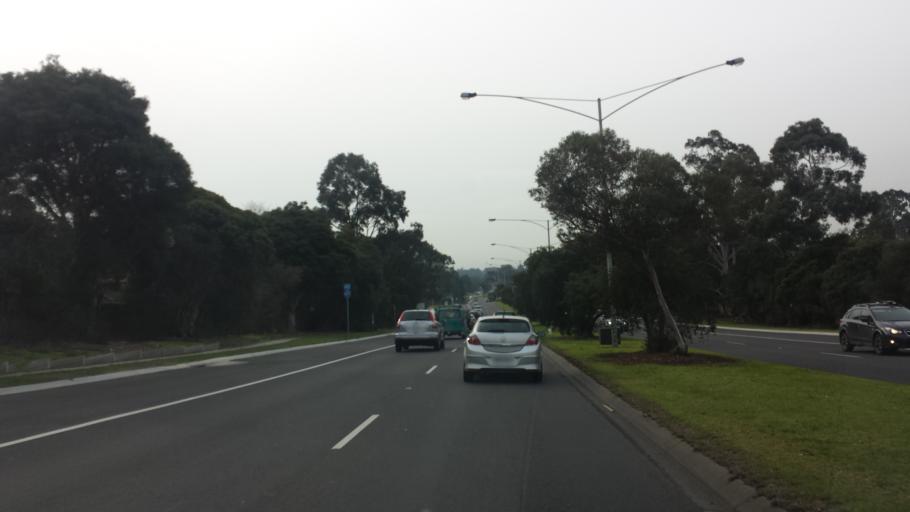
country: AU
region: Victoria
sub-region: Banyule
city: Darch
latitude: -37.7583
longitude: 145.1341
